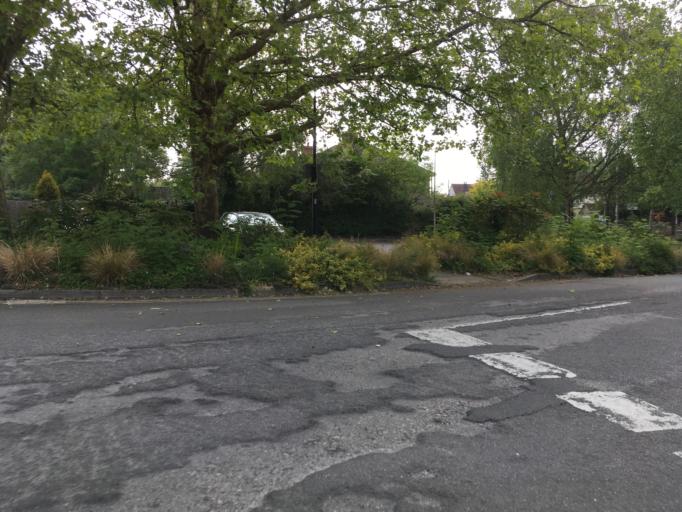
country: GB
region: England
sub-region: North Somerset
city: Nailsea
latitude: 51.4328
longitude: -2.7579
